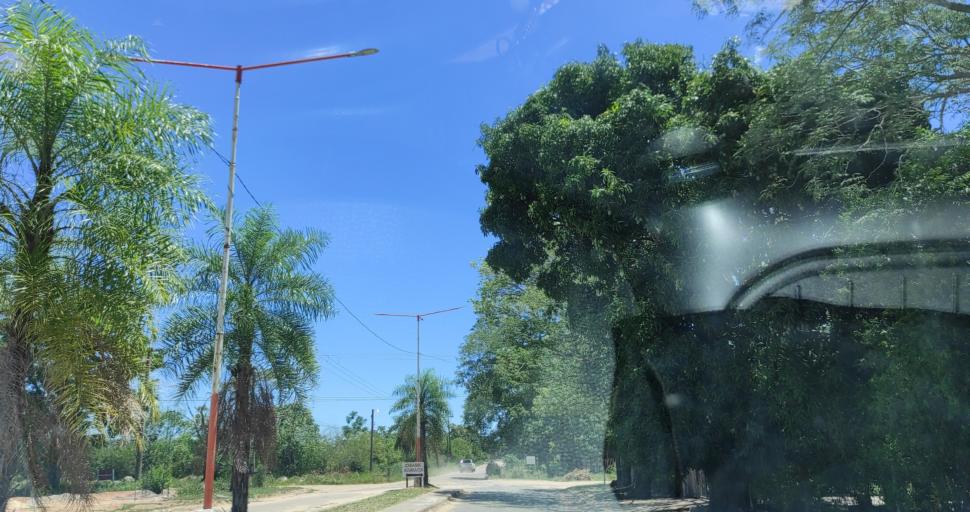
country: AR
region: Corrientes
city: Ituzaingo
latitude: -27.5955
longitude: -56.7052
